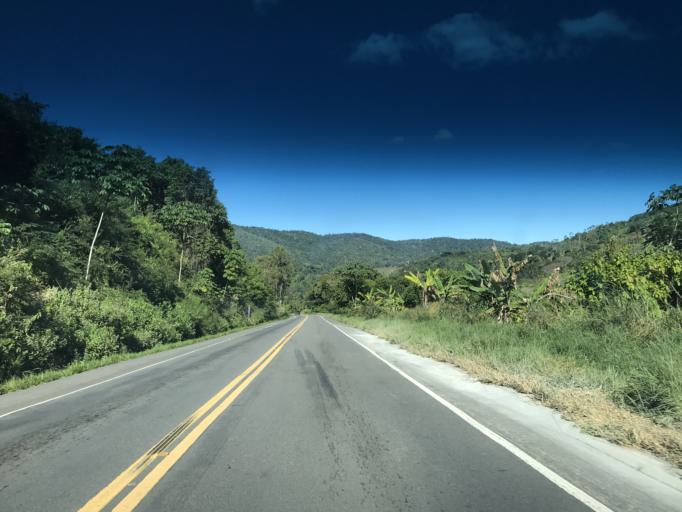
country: BR
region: Bahia
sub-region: Gandu
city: Gandu
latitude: -13.8823
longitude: -39.4881
